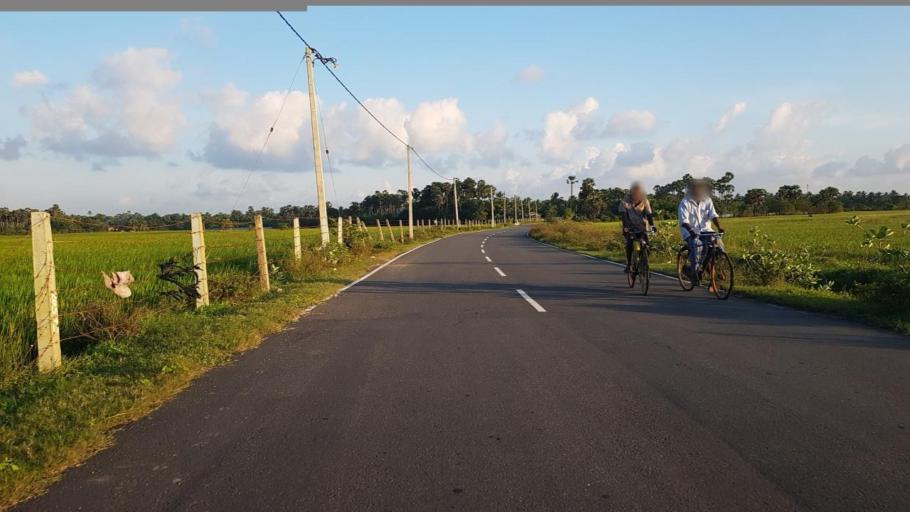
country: LK
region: Northern Province
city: Jaffna
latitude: 9.7252
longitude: 79.9758
